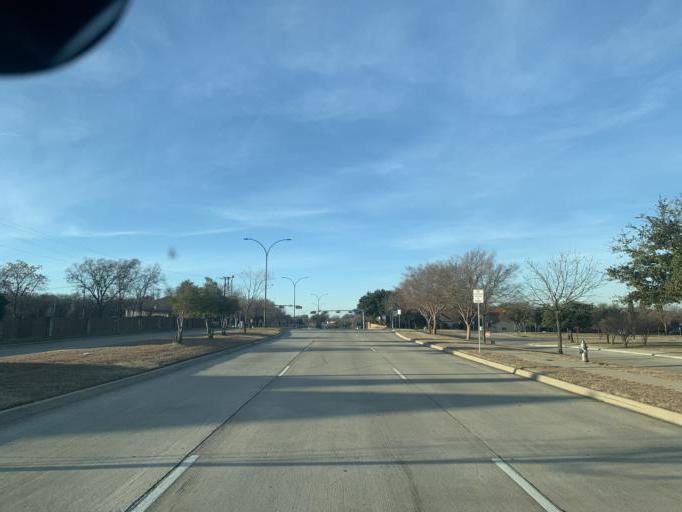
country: US
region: Texas
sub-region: Tarrant County
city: Arlington
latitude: 32.7803
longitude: -97.0720
